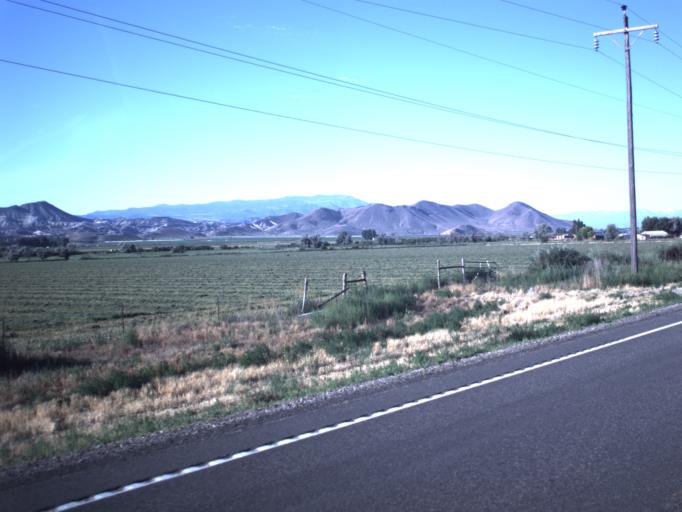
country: US
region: Utah
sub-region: Sevier County
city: Aurora
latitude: 38.9294
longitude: -111.9064
